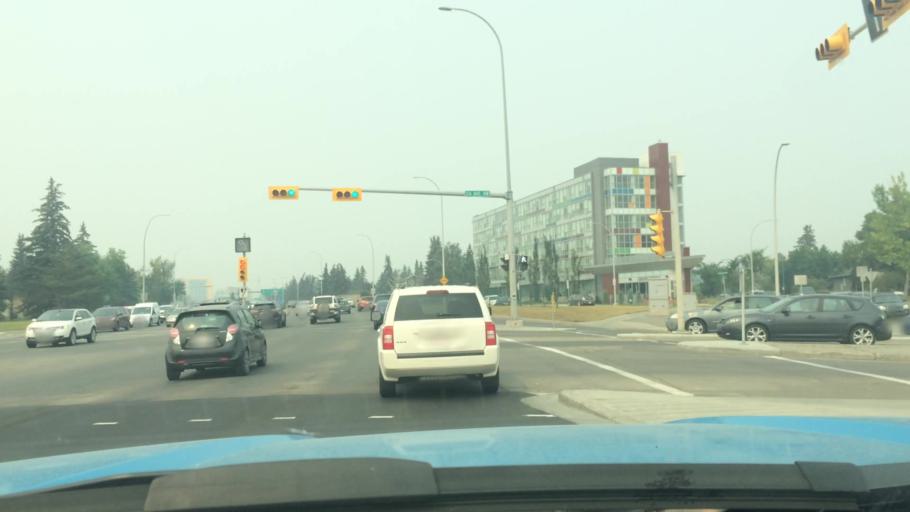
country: CA
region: Alberta
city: Calgary
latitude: 51.0741
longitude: -114.1181
